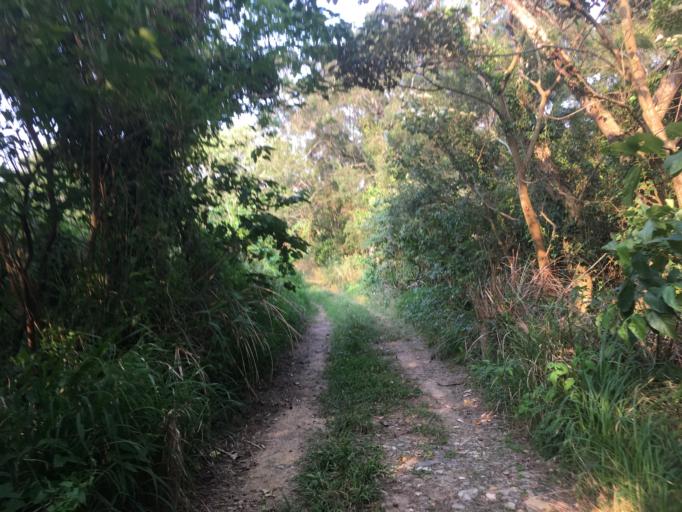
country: TW
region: Taiwan
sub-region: Hsinchu
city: Hsinchu
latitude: 24.7607
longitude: 120.9676
